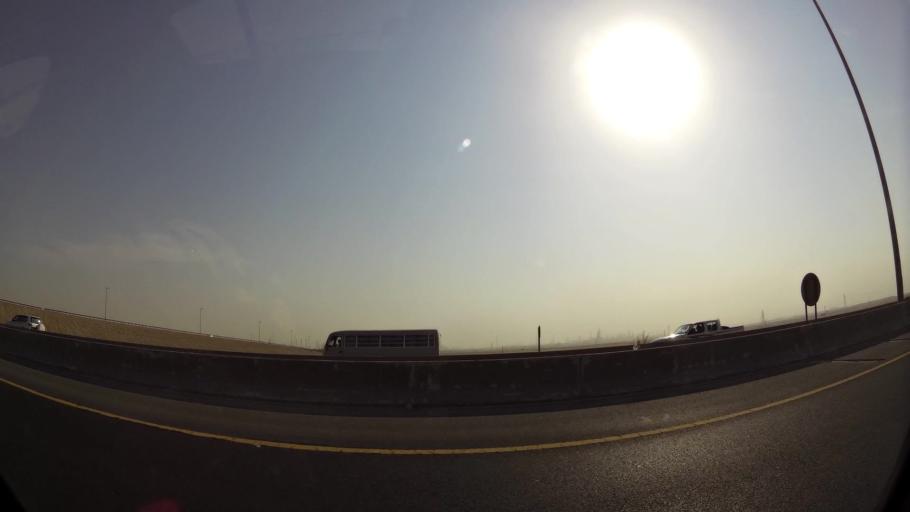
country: KW
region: Al Ahmadi
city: Al Ahmadi
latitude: 29.0454
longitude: 48.0945
